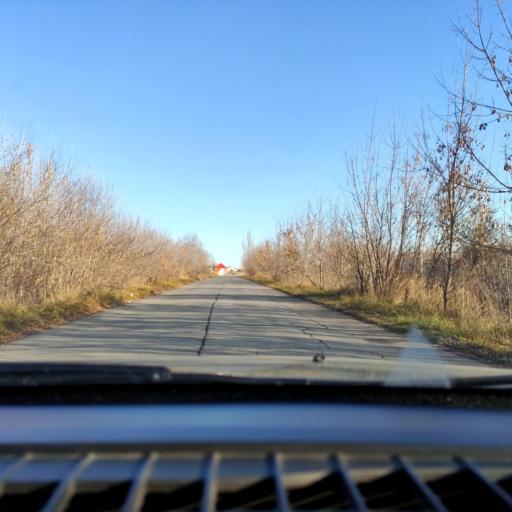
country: RU
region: Samara
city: Tol'yatti
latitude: 53.6628
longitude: 49.3356
